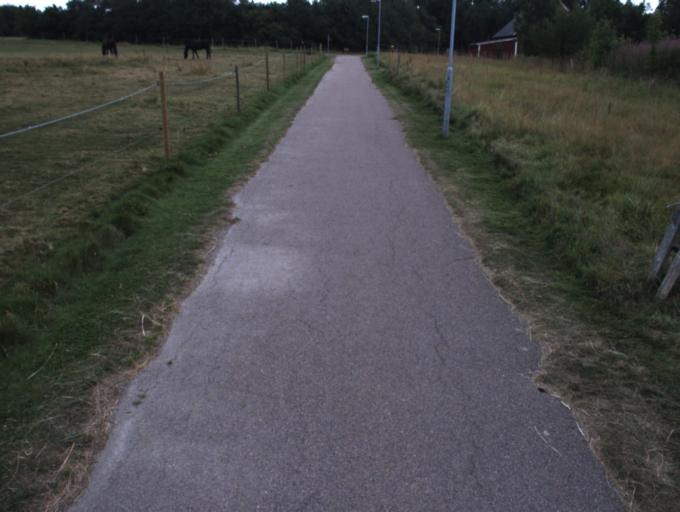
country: SE
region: Skane
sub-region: Helsingborg
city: Helsingborg
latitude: 56.0933
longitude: 12.6601
